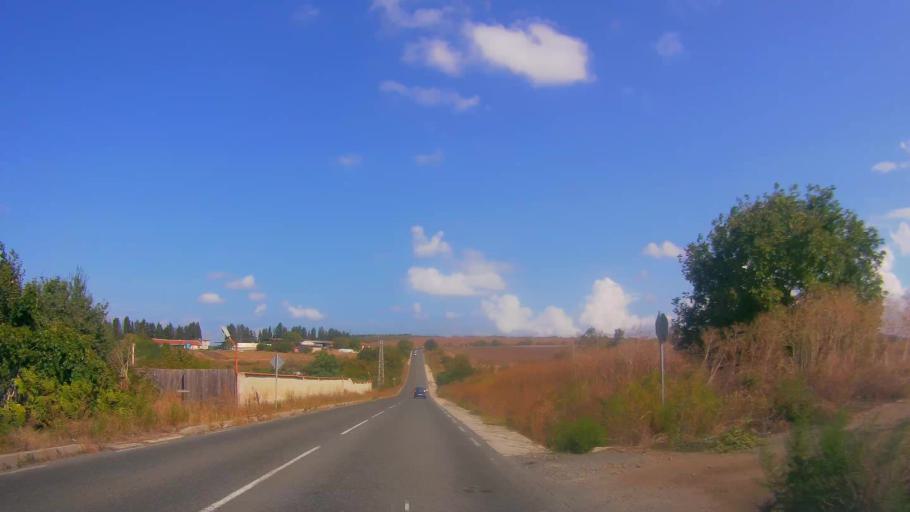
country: BG
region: Burgas
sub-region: Obshtina Burgas
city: Burgas
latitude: 42.4809
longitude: 27.3802
